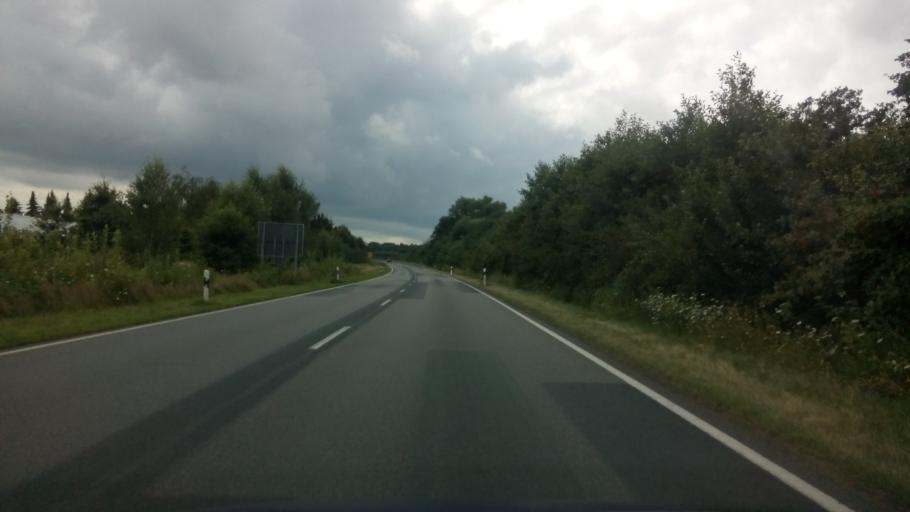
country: DE
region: Lower Saxony
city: Diepholz
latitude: 52.6176
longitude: 8.3637
